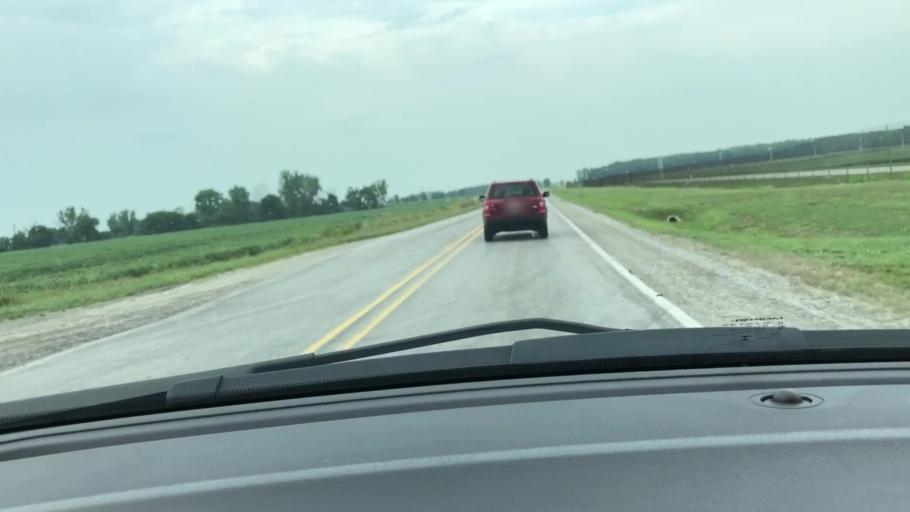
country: US
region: Michigan
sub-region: Saginaw County
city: Freeland
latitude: 43.5396
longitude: -84.0949
